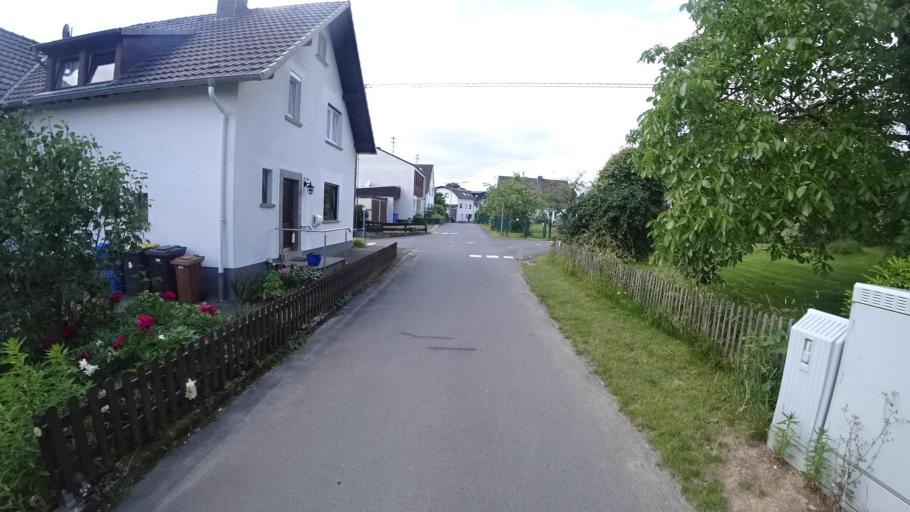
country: DE
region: Rheinland-Pfalz
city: Wolmersen
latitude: 50.7142
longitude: 7.6012
